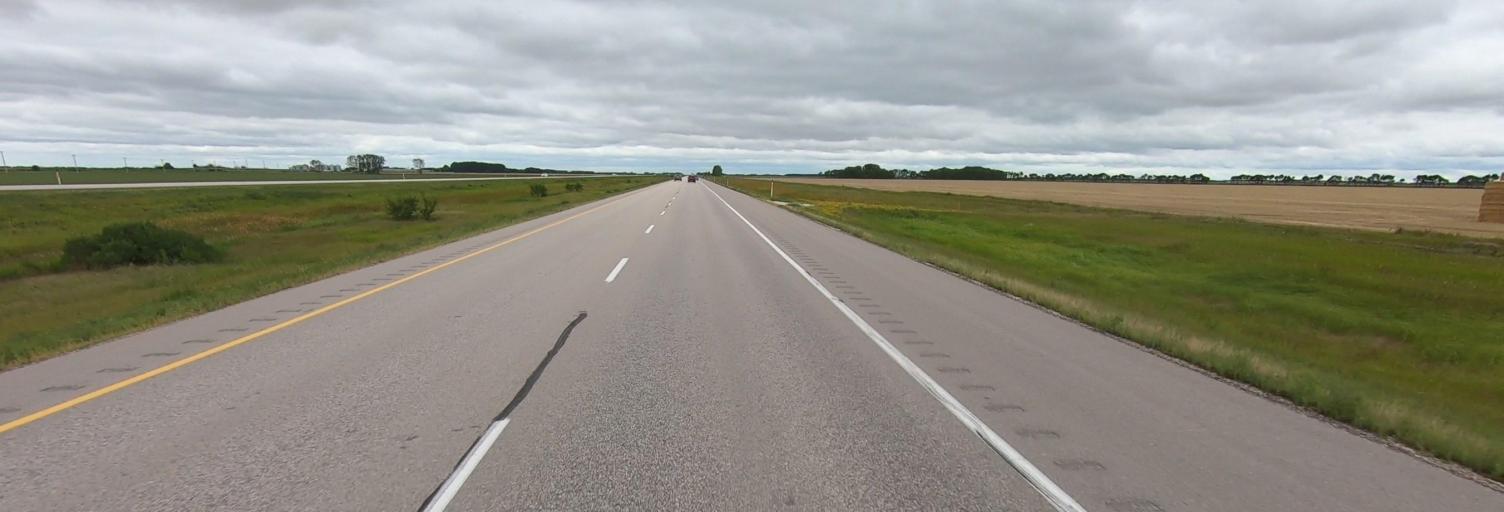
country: CA
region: Manitoba
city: Headingley
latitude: 49.9176
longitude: -97.8142
